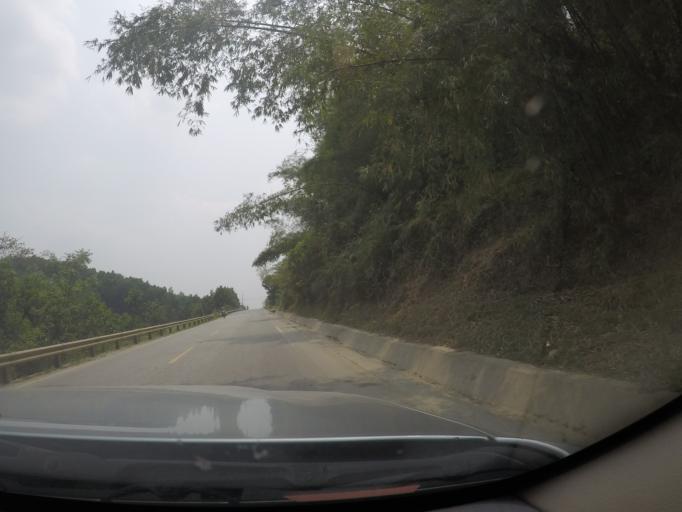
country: VN
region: Thanh Hoa
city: Thi Tran Yen Cat
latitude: 19.7846
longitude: 105.4025
